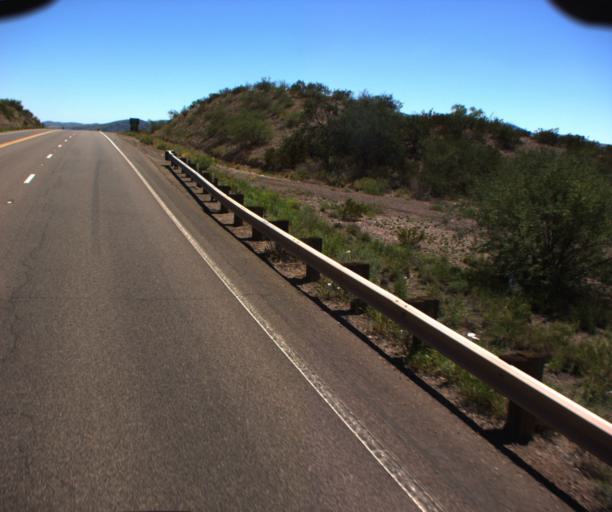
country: US
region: Arizona
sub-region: Greenlee County
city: Clifton
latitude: 33.0117
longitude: -109.2826
